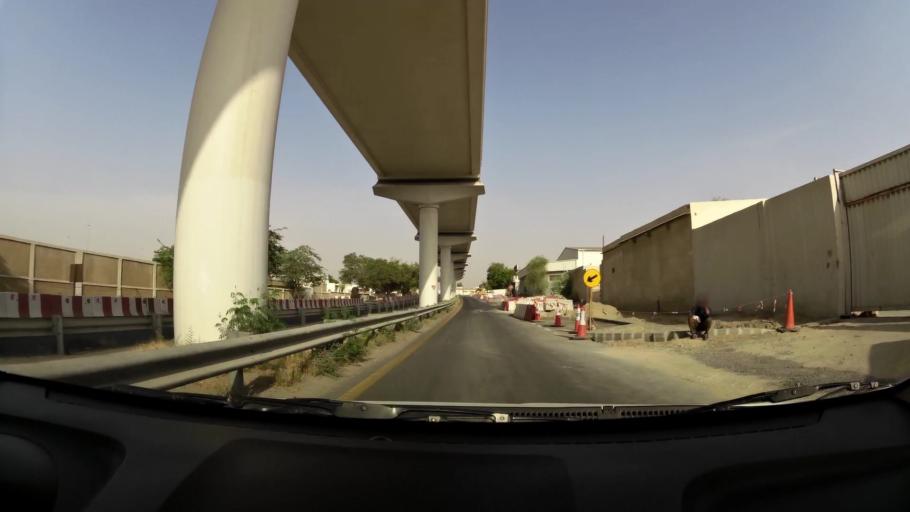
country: AE
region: Ash Shariqah
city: Sharjah
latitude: 25.2368
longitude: 55.3743
